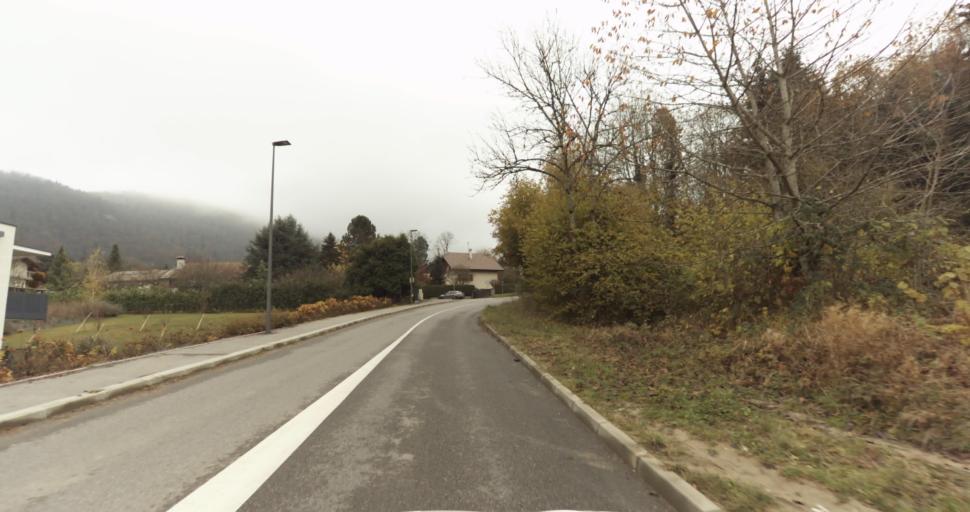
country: FR
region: Rhone-Alpes
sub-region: Departement de la Haute-Savoie
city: Seynod
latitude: 45.8556
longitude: 6.0892
